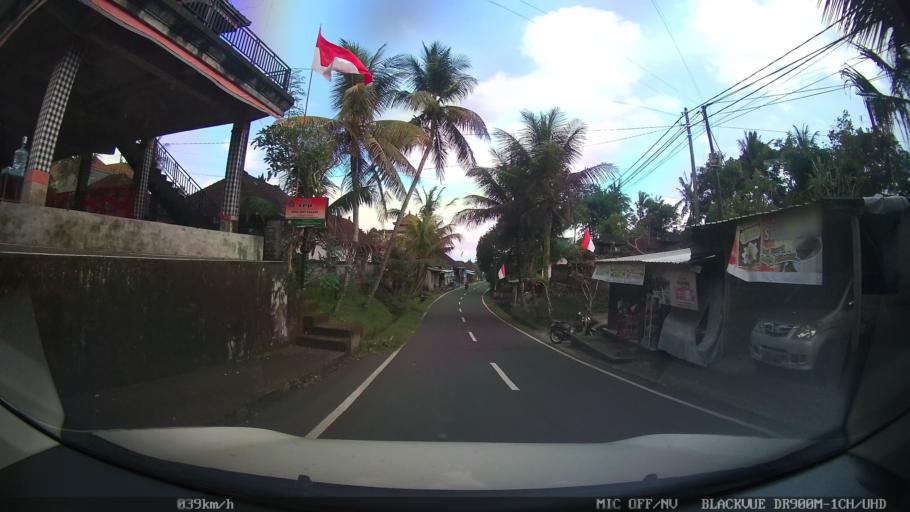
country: ID
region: Bali
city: Banjar Pesalakan
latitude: -8.4942
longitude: 115.2977
